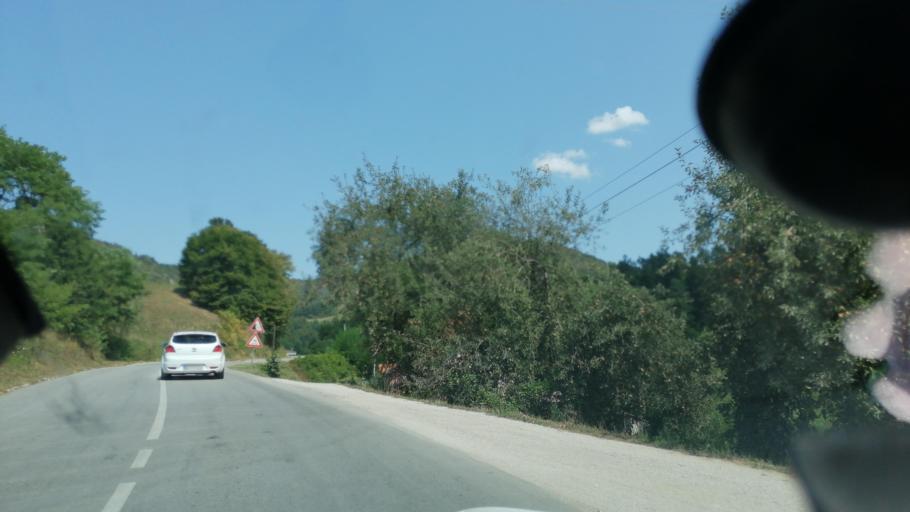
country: RS
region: Central Serbia
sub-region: Moravicki Okrug
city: Ivanjica
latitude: 43.6131
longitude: 20.2368
